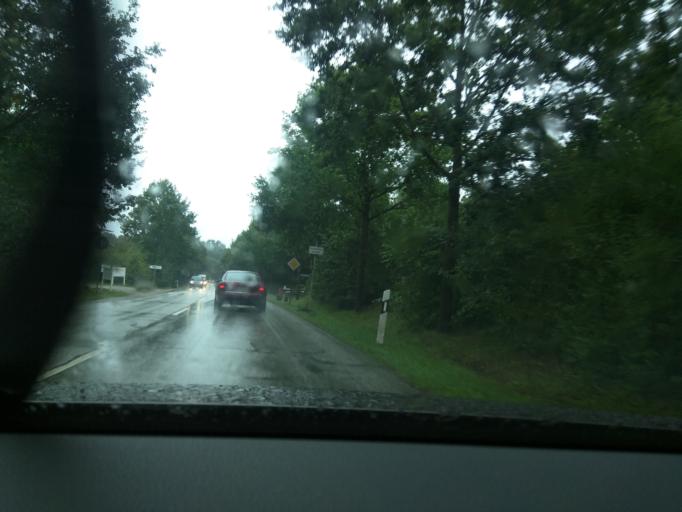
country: DE
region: Schleswig-Holstein
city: Schwarzenbek
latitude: 53.5143
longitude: 10.4757
